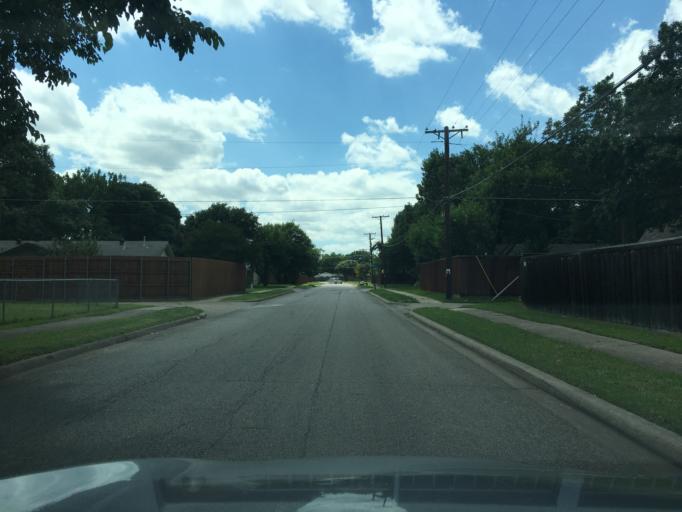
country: US
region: Texas
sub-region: Dallas County
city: Richardson
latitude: 32.9502
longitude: -96.7113
